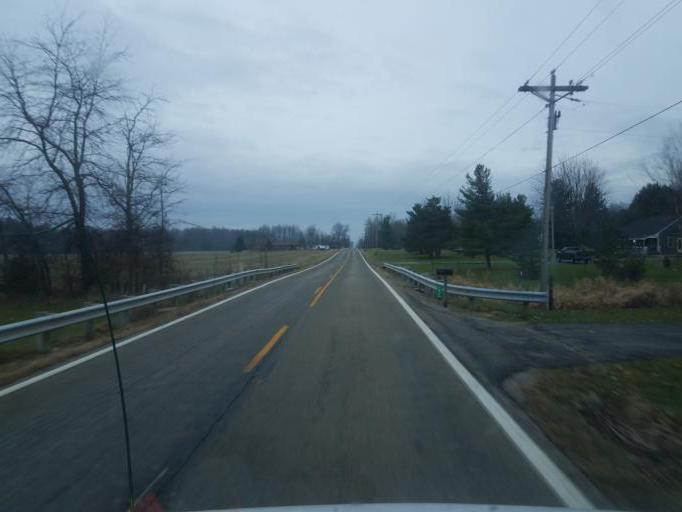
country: US
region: Ohio
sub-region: Morrow County
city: Cardington
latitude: 40.5538
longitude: -82.9624
